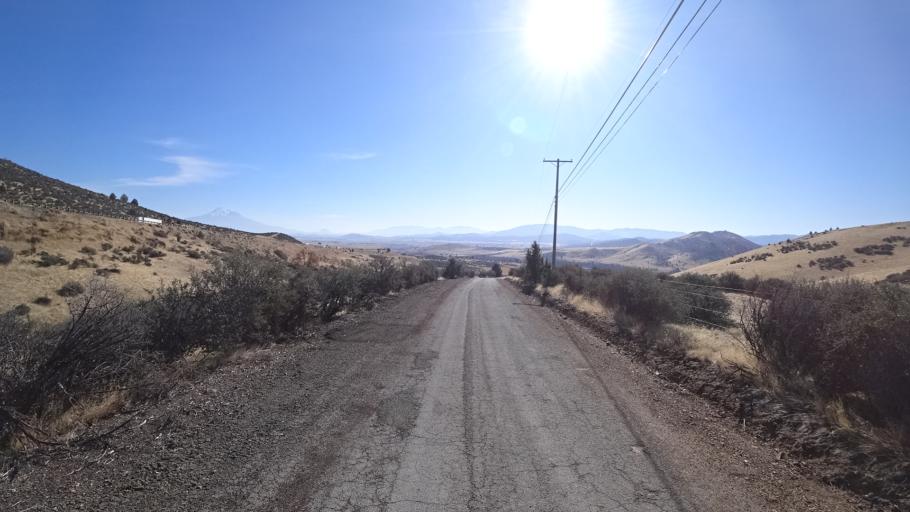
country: US
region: California
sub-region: Siskiyou County
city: Yreka
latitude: 41.7834
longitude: -122.5857
